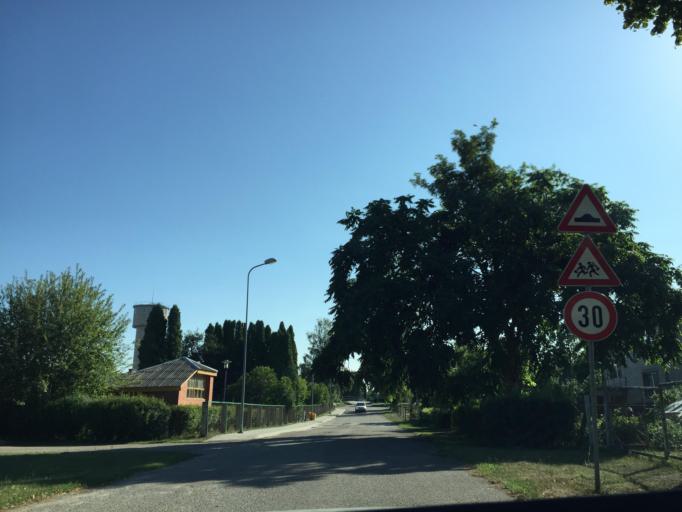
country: LV
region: Talsu Rajons
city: Sabile
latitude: 57.1294
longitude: 22.6500
